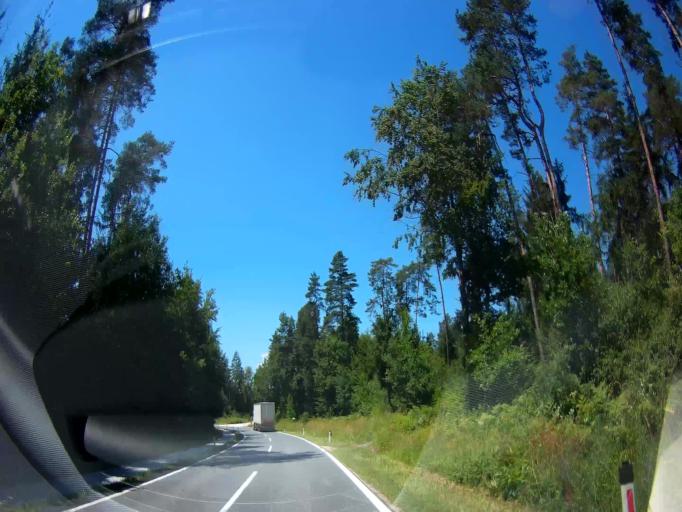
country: AT
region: Carinthia
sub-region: Politischer Bezirk Volkermarkt
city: Eberndorf
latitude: 46.6209
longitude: 14.6529
